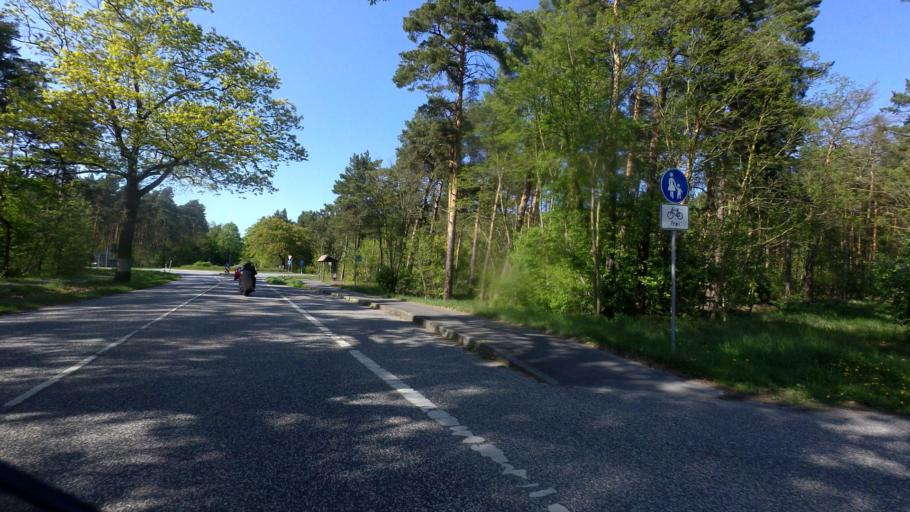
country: DE
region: Brandenburg
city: Bestensee
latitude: 52.2412
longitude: 13.6641
